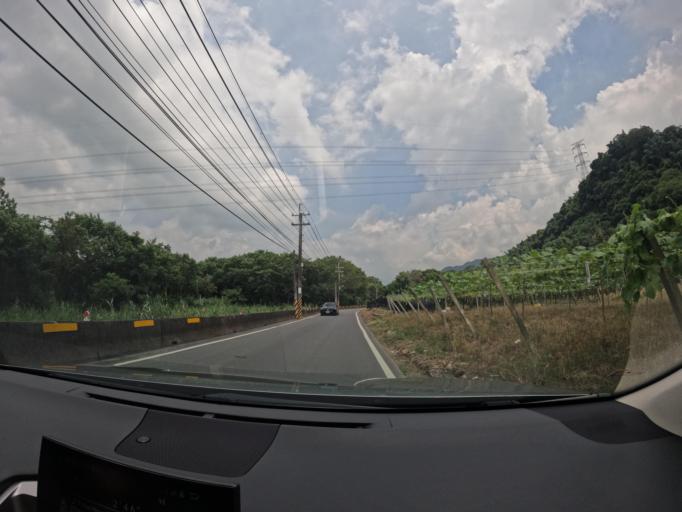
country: TW
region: Taiwan
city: Lugu
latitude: 23.8113
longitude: 120.8185
